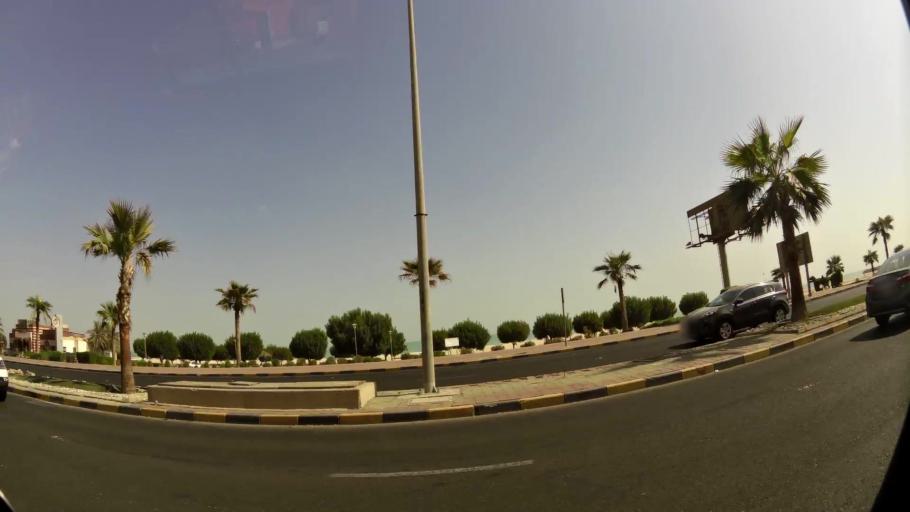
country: KW
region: Muhafazat Hawalli
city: As Salimiyah
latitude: 29.3324
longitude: 48.0925
